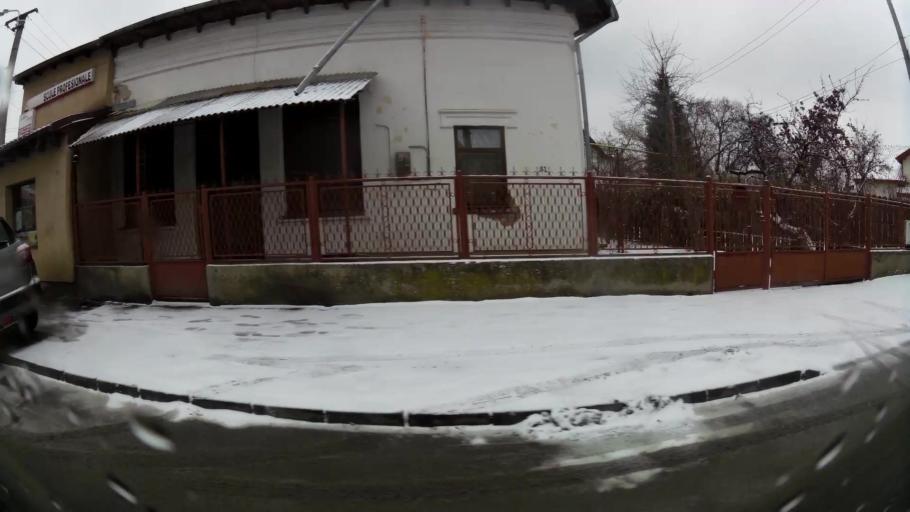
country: RO
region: Prahova
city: Ploiesti
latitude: 44.9297
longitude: 26.0184
